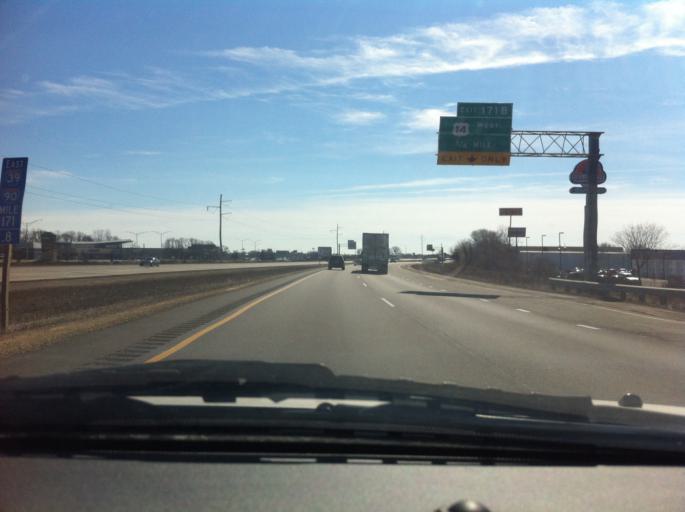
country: US
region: Wisconsin
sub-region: Rock County
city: Milton
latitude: 42.7731
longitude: -89.0049
